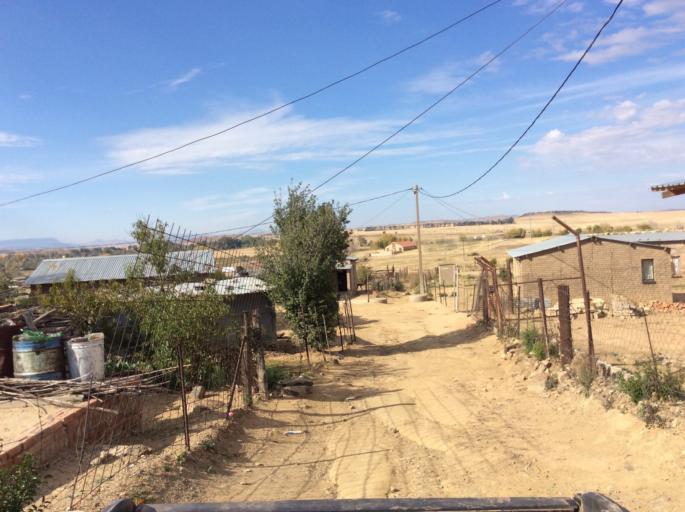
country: LS
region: Mafeteng
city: Mafeteng
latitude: -29.7189
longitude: 27.0151
